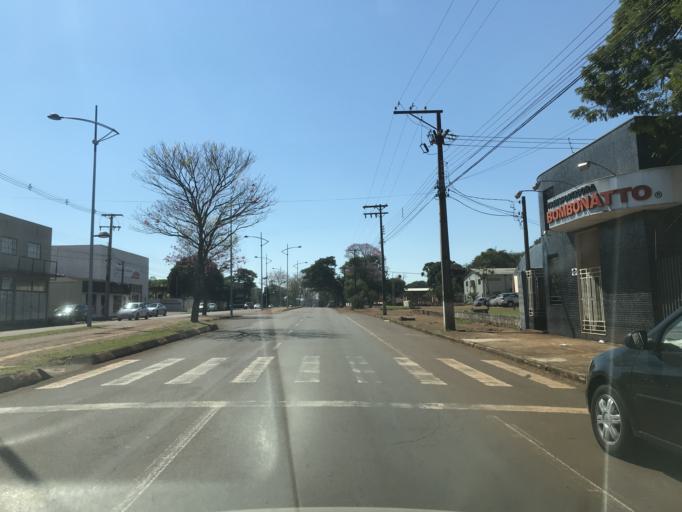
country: BR
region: Parana
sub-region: Toledo
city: Toledo
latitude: -24.7239
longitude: -53.7220
